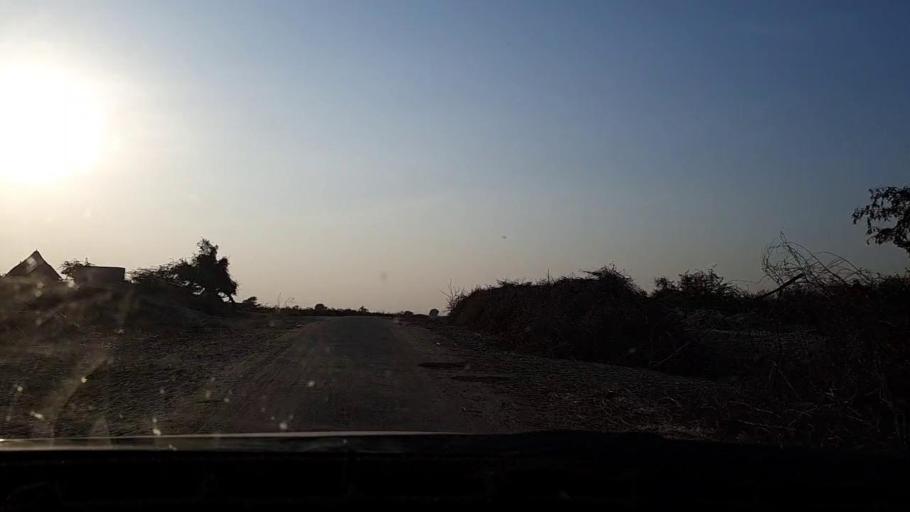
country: PK
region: Sindh
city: Tando Mittha Khan
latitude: 25.8658
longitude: 69.2690
